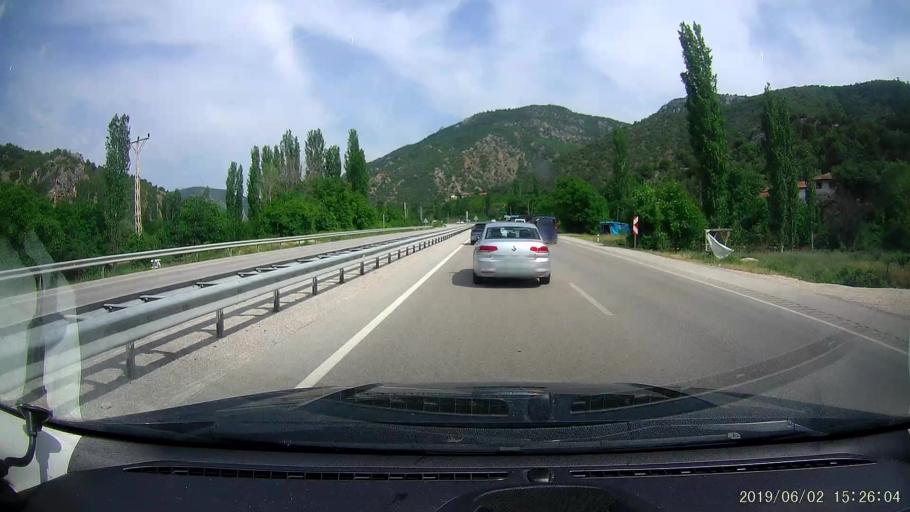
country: TR
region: Amasya
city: Saraycik
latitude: 40.9883
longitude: 35.0304
